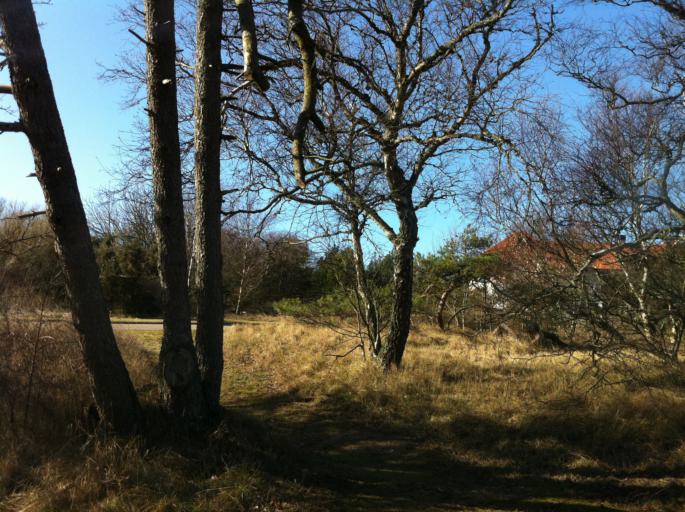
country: SE
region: Skane
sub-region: Angelholms Kommun
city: AEngelholm
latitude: 56.2637
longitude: 12.8371
